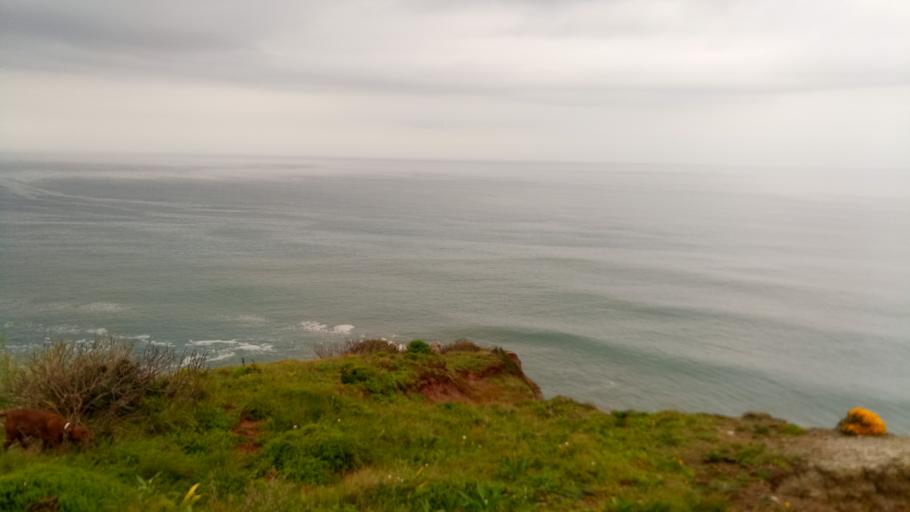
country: PT
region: Leiria
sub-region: Caldas da Rainha
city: Caldas da Rainha
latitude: 39.4736
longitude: -9.2005
